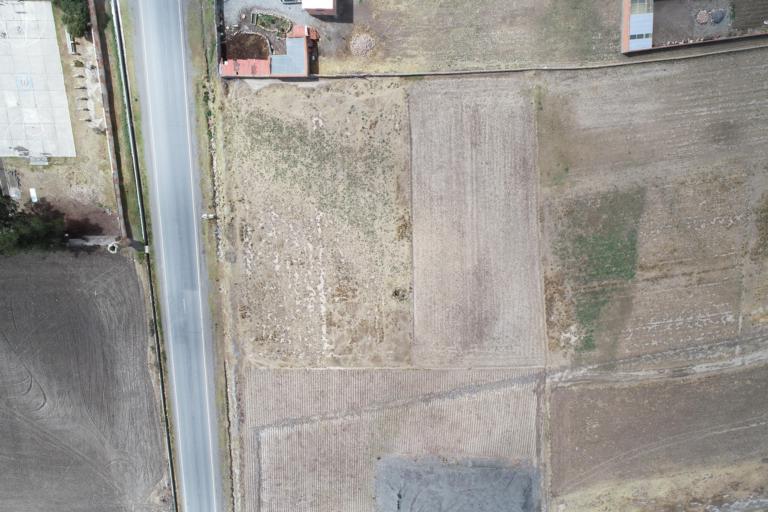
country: BO
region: La Paz
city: Achacachi
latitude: -16.0311
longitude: -68.6891
